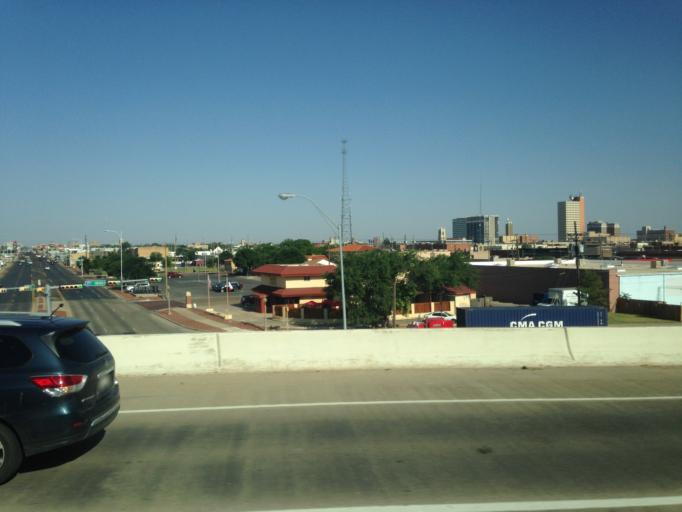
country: US
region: Texas
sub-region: Lubbock County
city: Lubbock
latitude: 33.5782
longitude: -101.8407
